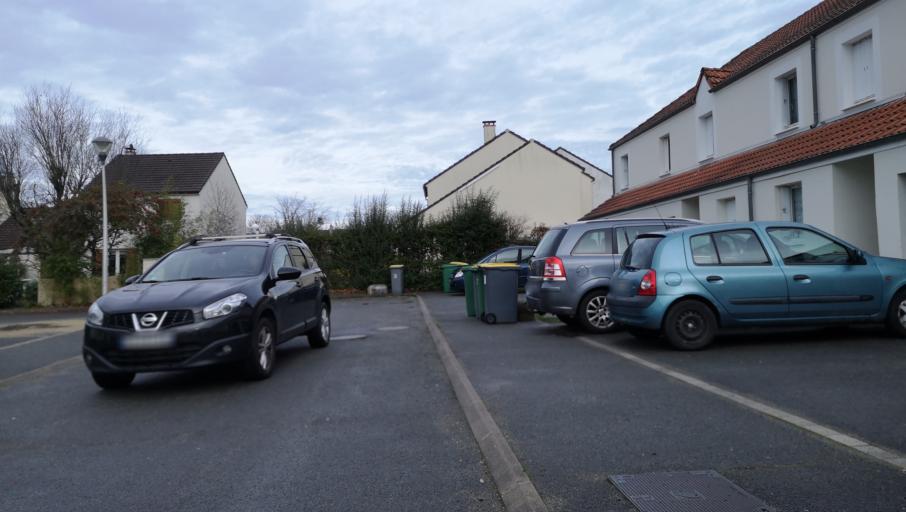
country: FR
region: Centre
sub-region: Departement du Loiret
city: Saint-Jean-de-Braye
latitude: 47.9076
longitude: 1.9572
